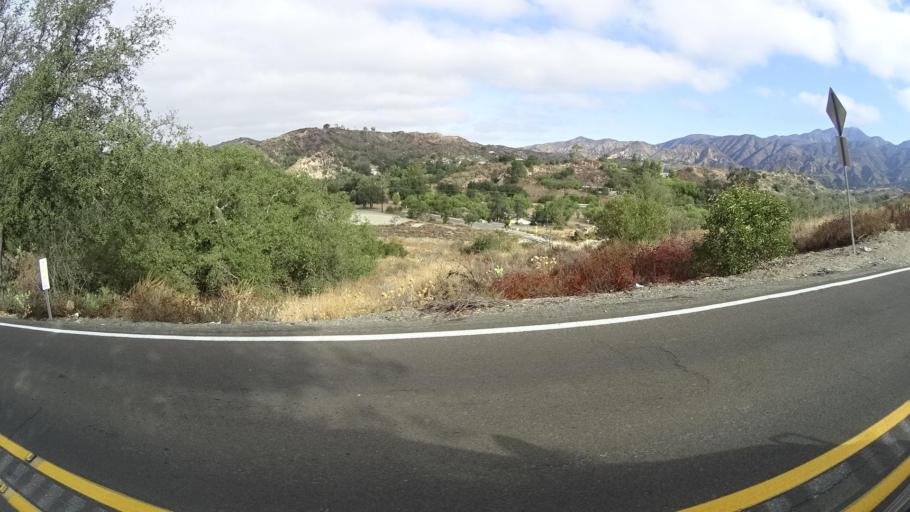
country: US
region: California
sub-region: Orange County
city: Trabuco Canyon
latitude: 33.6572
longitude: -117.5835
